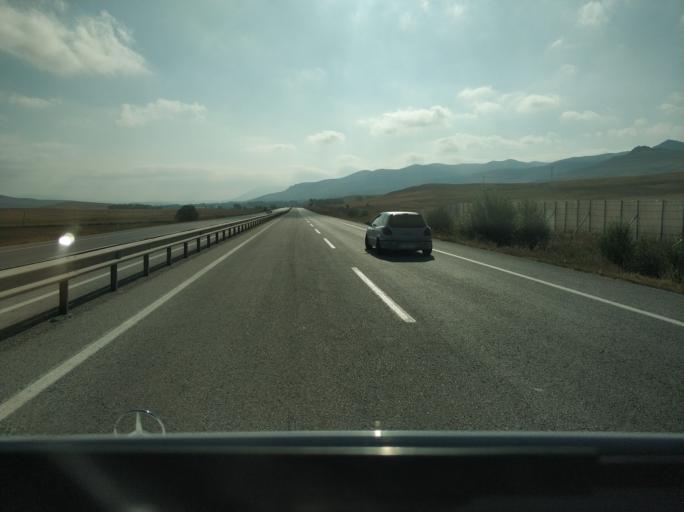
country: TR
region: Sivas
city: Yildizeli
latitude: 39.8353
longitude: 36.4319
